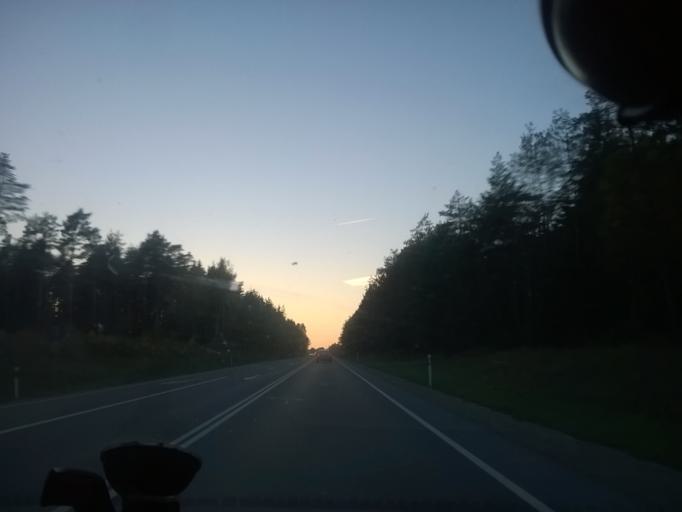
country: EE
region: Laeaene
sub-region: Lihula vald
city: Lihula
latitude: 58.9736
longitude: 23.9146
